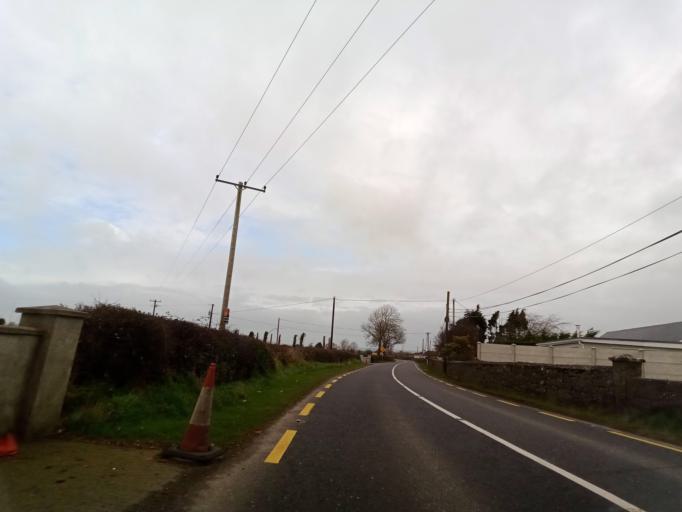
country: IE
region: Leinster
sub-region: Kilkenny
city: Kilkenny
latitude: 52.7186
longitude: -7.2939
